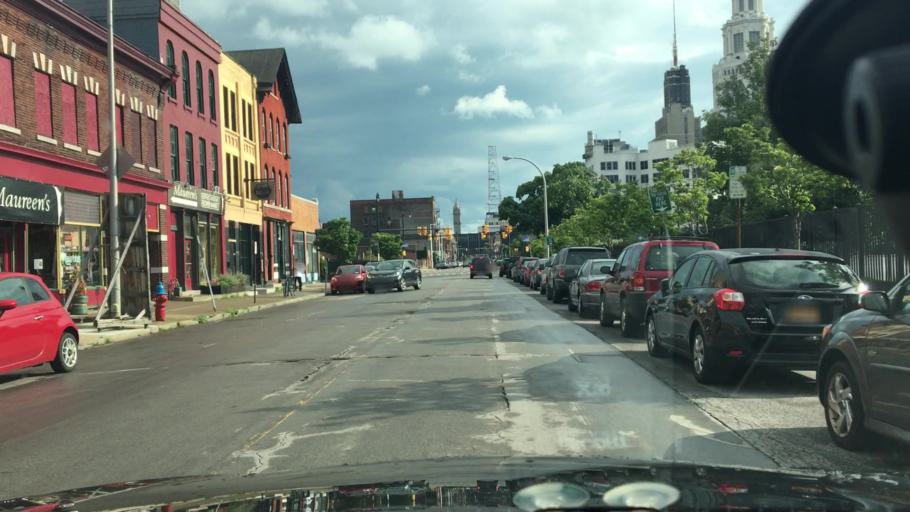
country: US
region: New York
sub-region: Erie County
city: Buffalo
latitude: 42.8906
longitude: -78.8705
